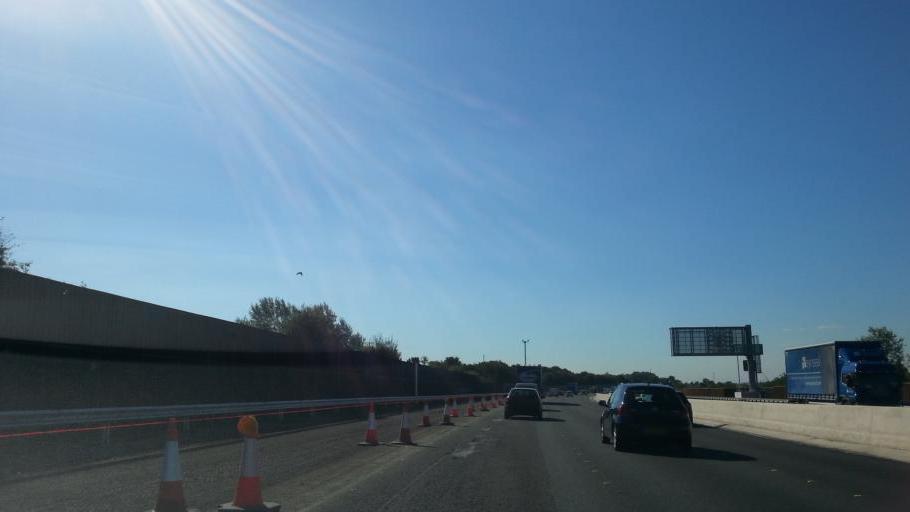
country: GB
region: England
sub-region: Derbyshire
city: Long Eaton
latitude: 52.8948
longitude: -1.2992
